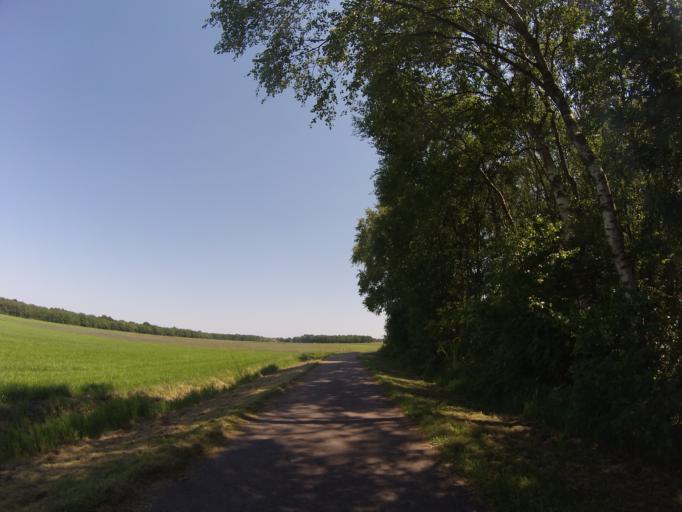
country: NL
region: Drenthe
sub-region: Gemeente Emmen
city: Schoonebeek
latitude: 52.6900
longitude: 6.8417
